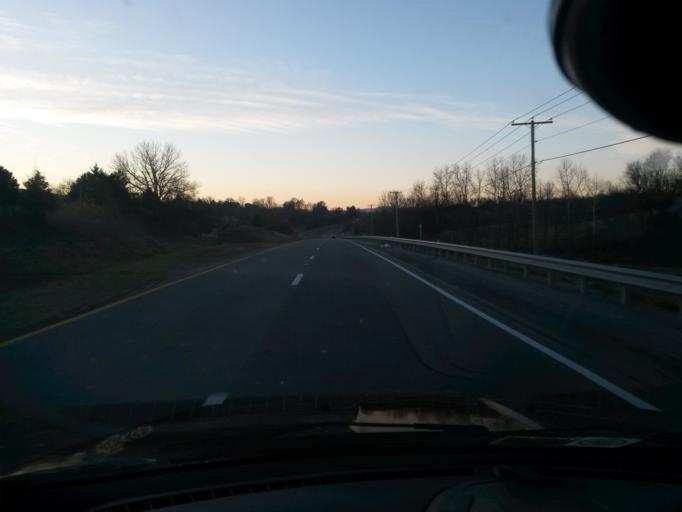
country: US
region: Virginia
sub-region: Botetourt County
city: Daleville
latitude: 37.4419
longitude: -79.9045
